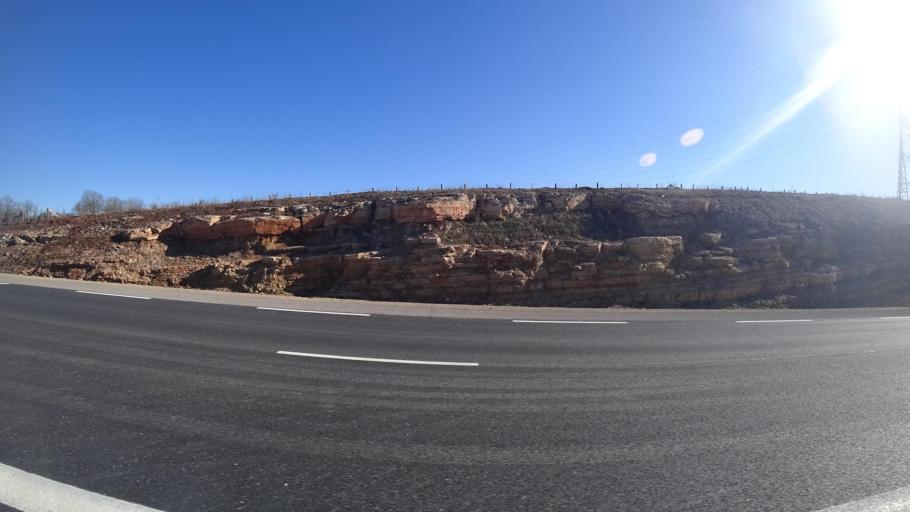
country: FR
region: Midi-Pyrenees
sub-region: Departement de l'Aveyron
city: Sebazac-Concoures
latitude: 44.3906
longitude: 2.6137
